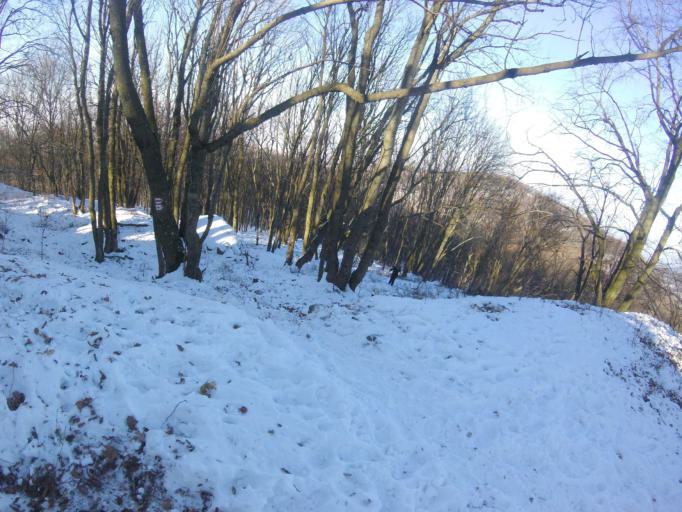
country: SK
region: Nitriansky
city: Sahy
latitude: 47.9601
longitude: 18.8789
